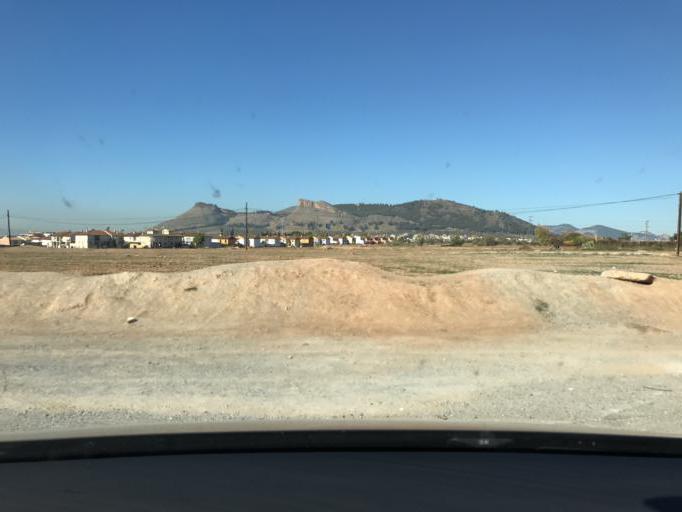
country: ES
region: Andalusia
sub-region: Provincia de Granada
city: Albolote
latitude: 37.2349
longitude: -3.6515
